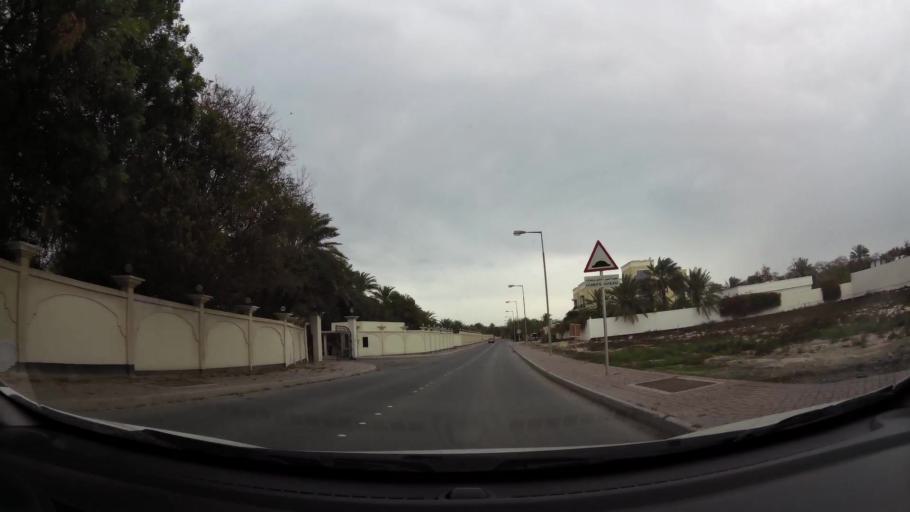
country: BH
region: Central Governorate
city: Madinat Hamad
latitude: 26.1488
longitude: 50.4553
